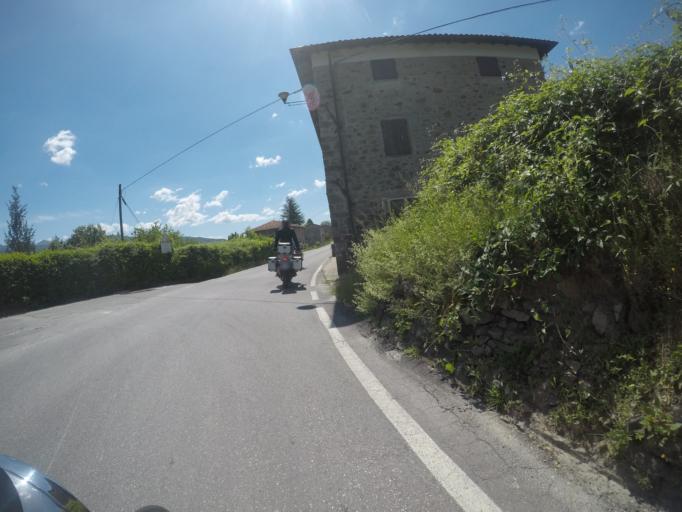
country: IT
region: Tuscany
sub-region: Provincia di Lucca
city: Pieve Fosciana
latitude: 44.1294
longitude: 10.3822
